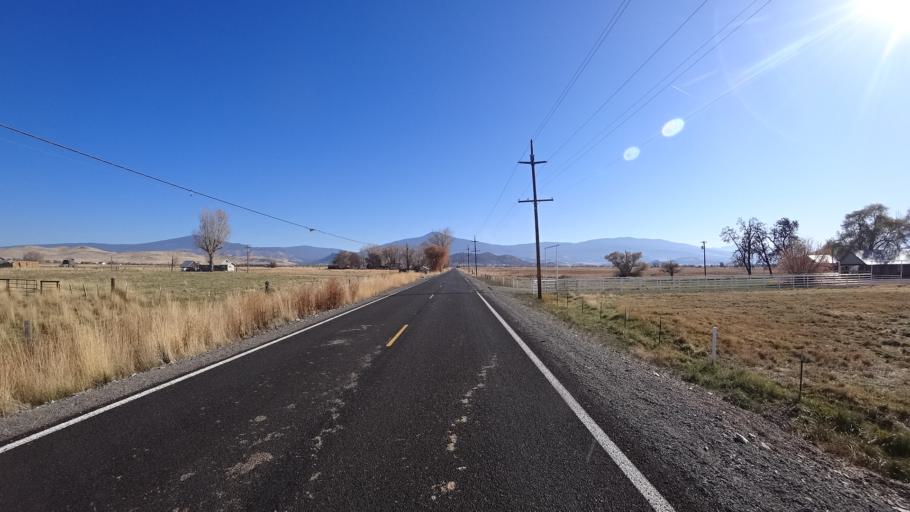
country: US
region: California
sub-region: Siskiyou County
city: Montague
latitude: 41.7114
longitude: -122.4158
